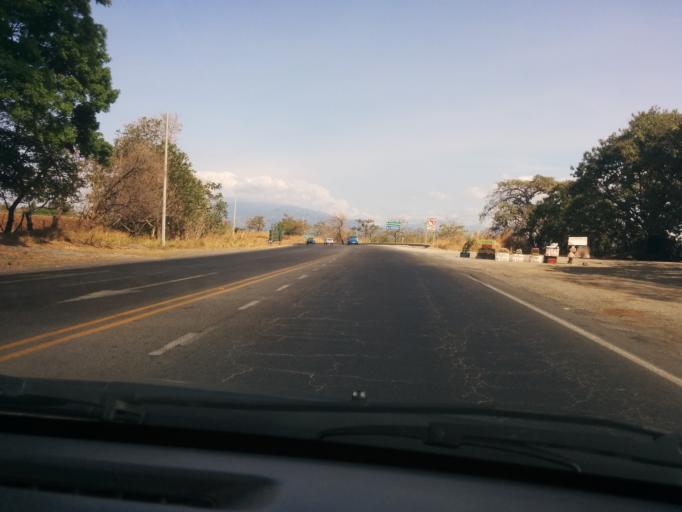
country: CR
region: Alajuela
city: Atenas
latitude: 10.0179
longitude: -84.3559
